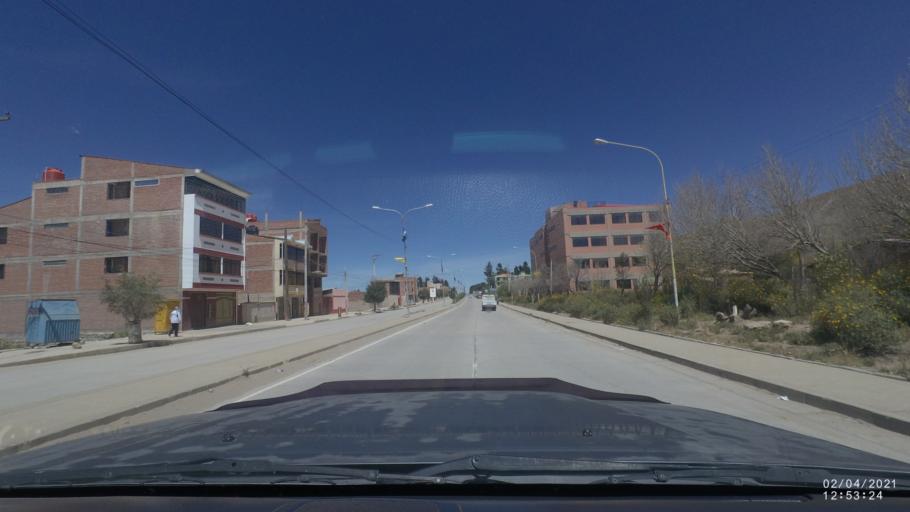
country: BO
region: Oruro
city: Oruro
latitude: -17.9912
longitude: -67.1352
